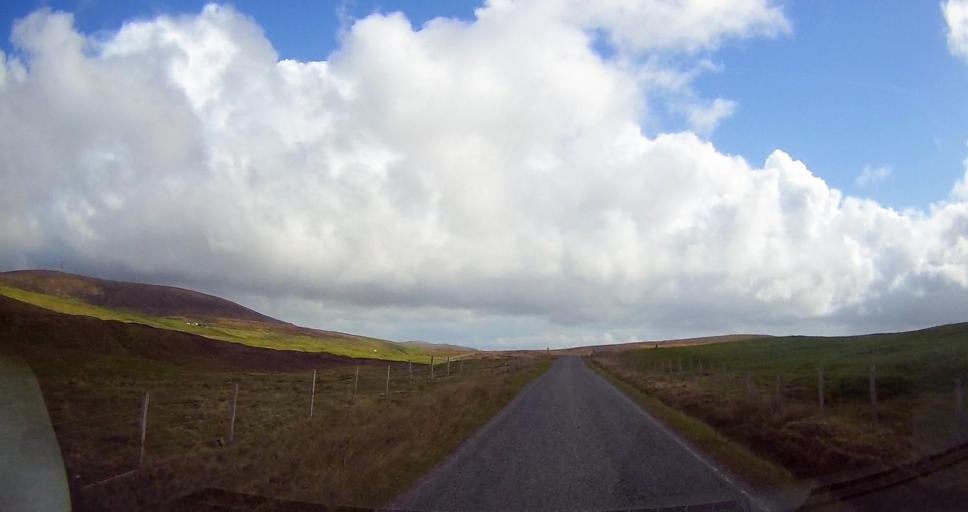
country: GB
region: Scotland
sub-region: Shetland Islands
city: Lerwick
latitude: 60.5129
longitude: -1.3844
